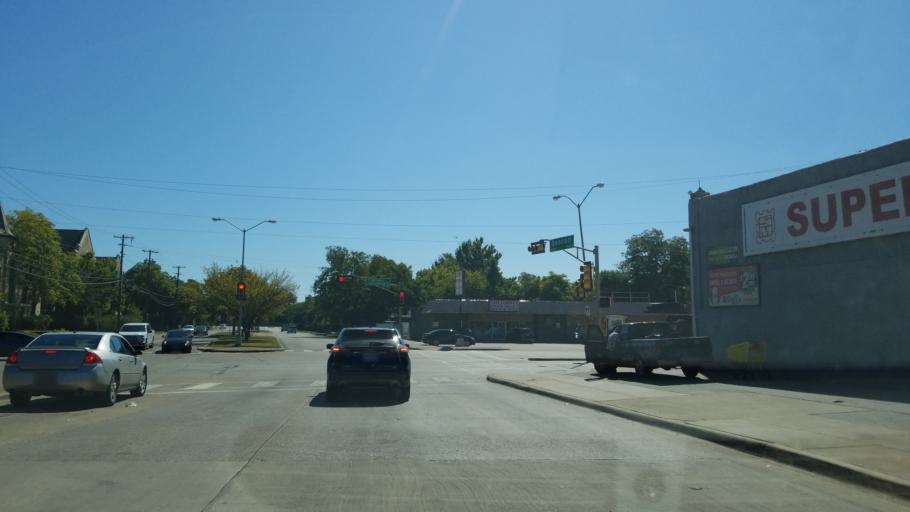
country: US
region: Texas
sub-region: Dallas County
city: Highland Park
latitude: 32.8014
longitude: -96.7567
